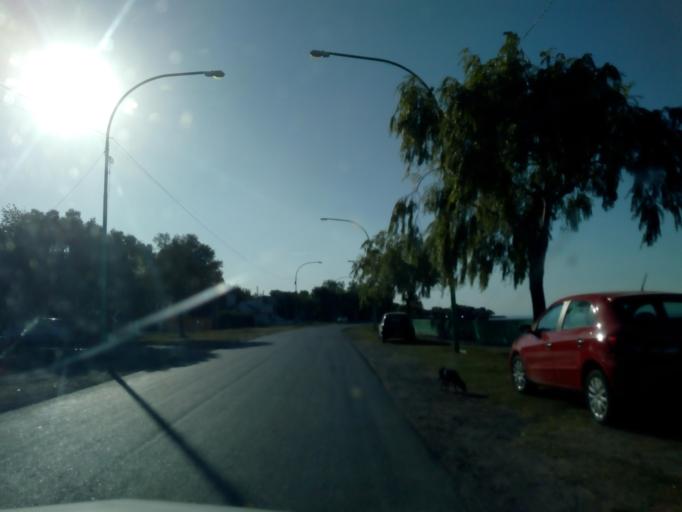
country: AR
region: Buenos Aires
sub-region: Partido de Ensenada
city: Ensenada
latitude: -34.7994
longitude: -57.9895
